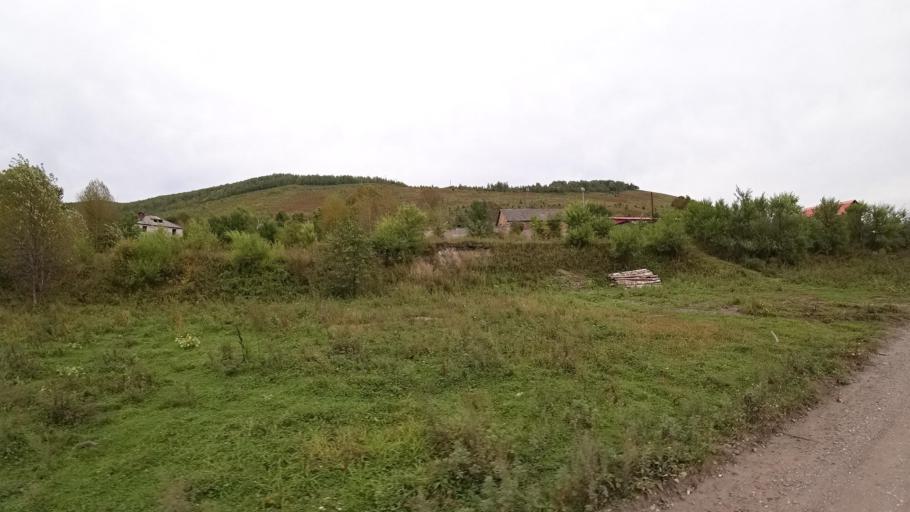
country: RU
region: Jewish Autonomous Oblast
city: Khingansk
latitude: 49.0316
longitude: 131.0565
